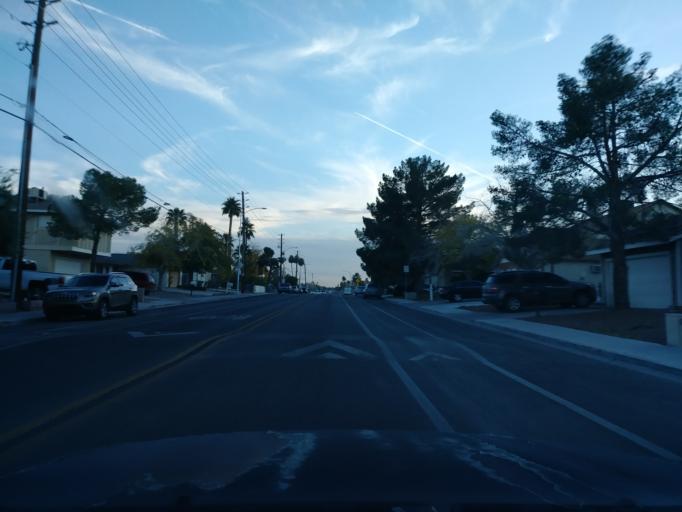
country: US
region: Nevada
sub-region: Clark County
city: Spring Valley
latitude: 36.1682
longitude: -115.2422
